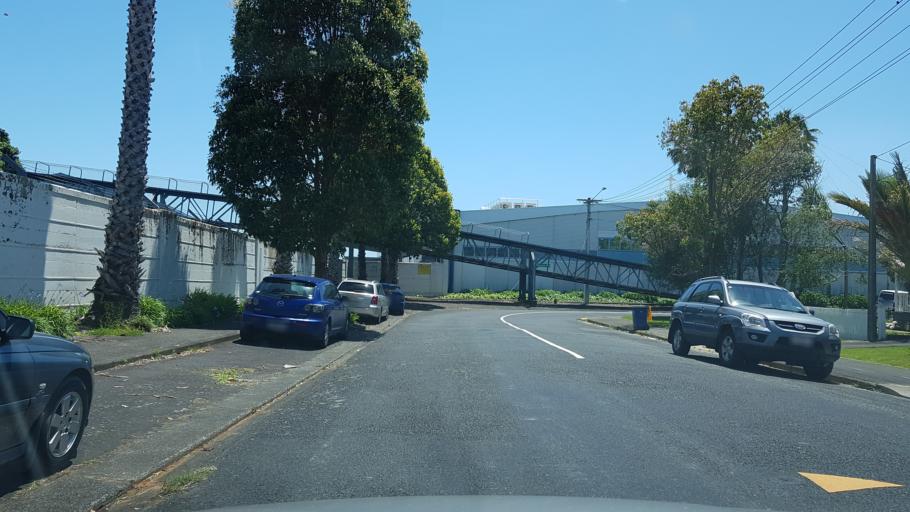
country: NZ
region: Auckland
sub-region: Auckland
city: Auckland
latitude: -36.8265
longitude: 174.7893
